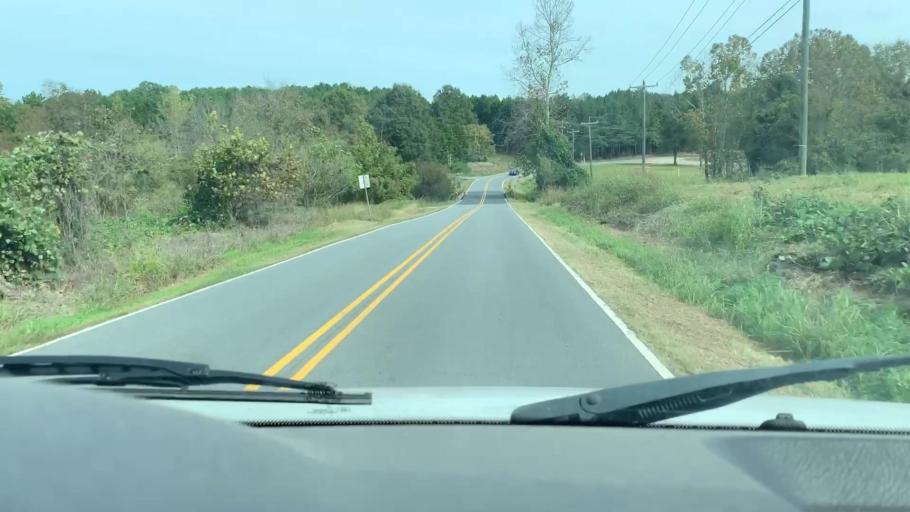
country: US
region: North Carolina
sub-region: Mecklenburg County
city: Huntersville
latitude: 35.4236
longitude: -80.7660
